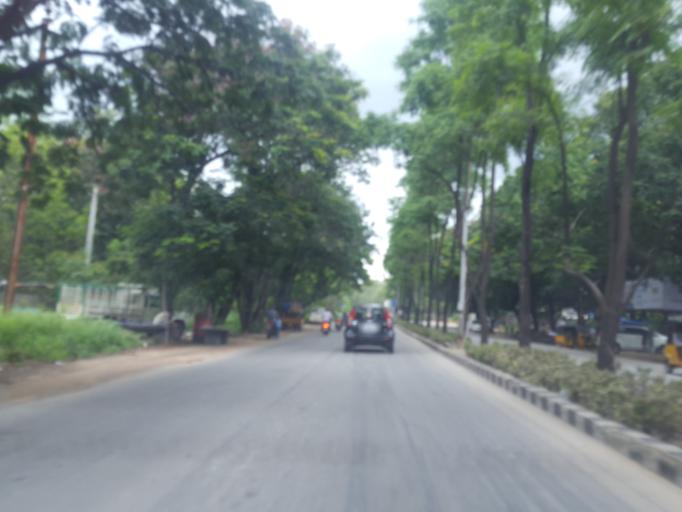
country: IN
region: Telangana
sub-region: Medak
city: Serilingampalle
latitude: 17.4590
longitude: 78.3382
